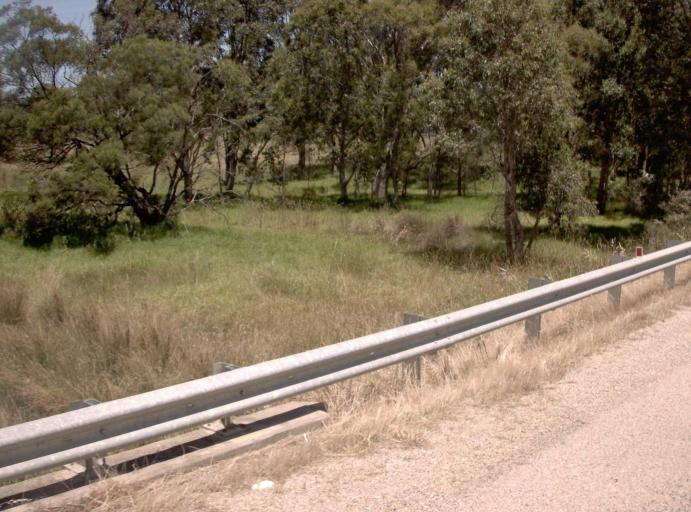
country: AU
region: Victoria
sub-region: East Gippsland
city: Bairnsdale
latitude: -37.7606
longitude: 147.7044
